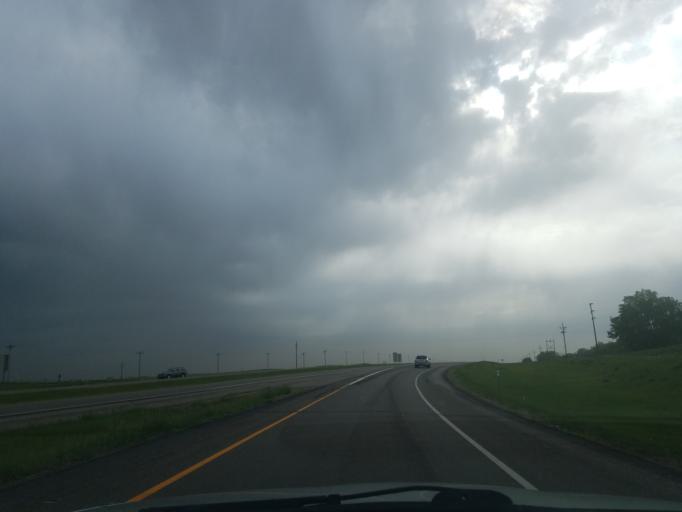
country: US
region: North Dakota
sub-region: Kidder County
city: Steele
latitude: 46.8368
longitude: -100.2917
